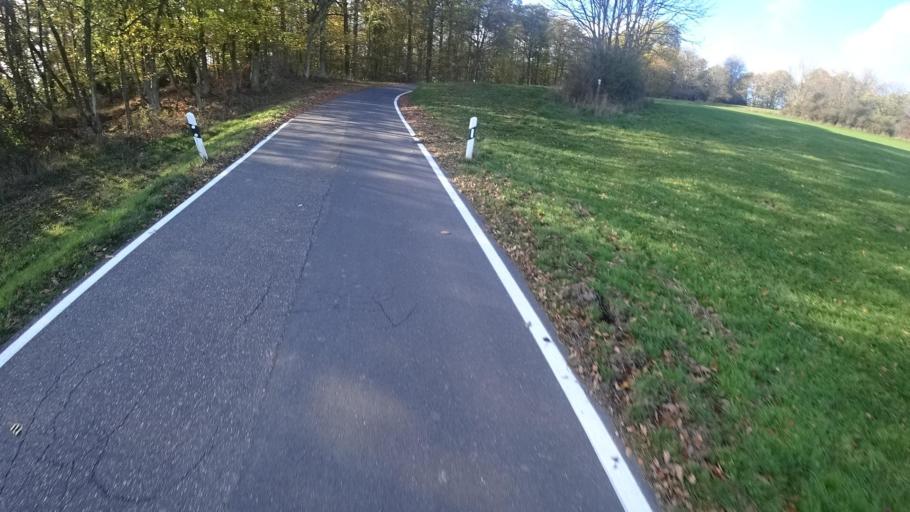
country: DE
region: Rheinland-Pfalz
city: Berg
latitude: 50.5230
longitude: 6.9516
